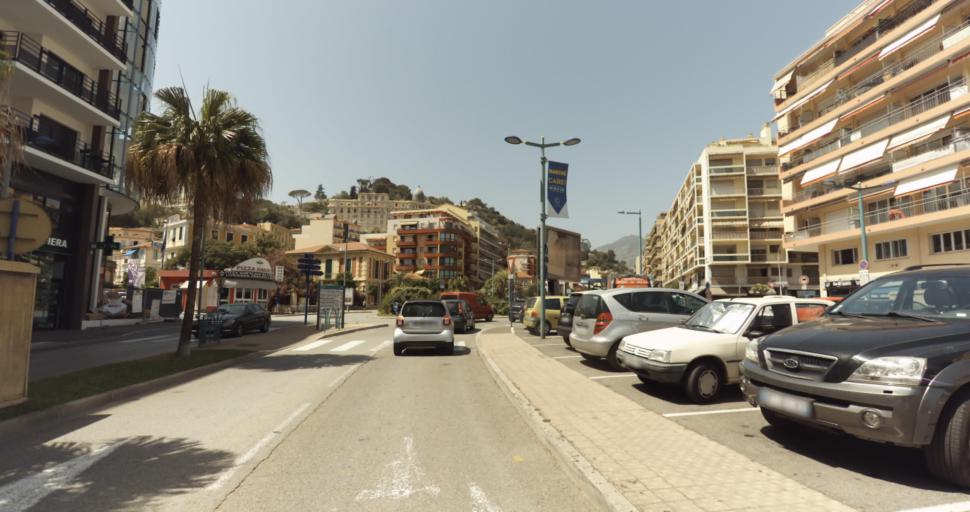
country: FR
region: Provence-Alpes-Cote d'Azur
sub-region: Departement des Alpes-Maritimes
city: Menton
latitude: 43.7762
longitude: 7.4945
